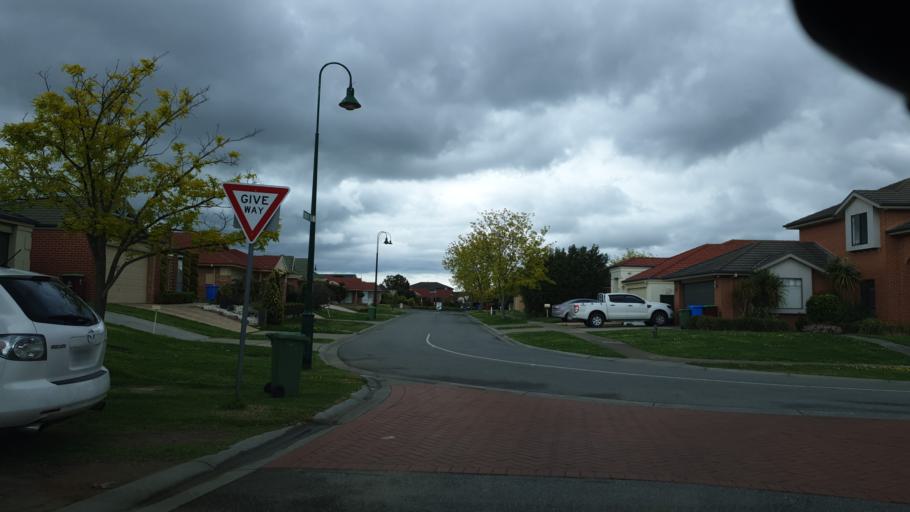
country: AU
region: Victoria
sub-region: Casey
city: Cranbourne North
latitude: -38.0654
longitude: 145.2885
